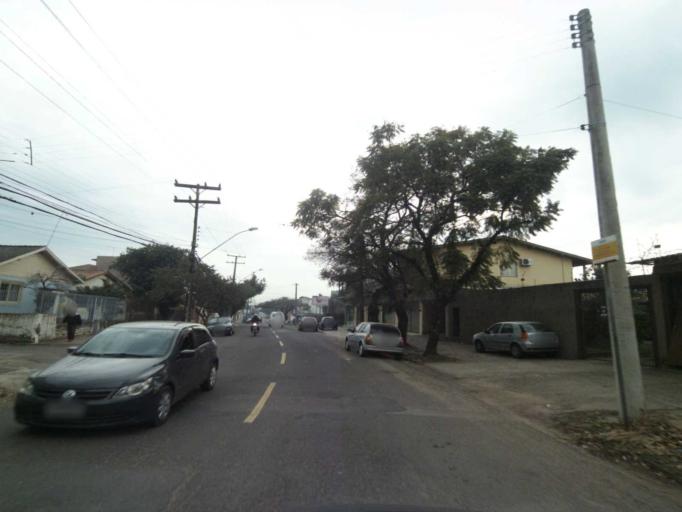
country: BR
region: Rio Grande do Sul
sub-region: Sao Leopoldo
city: Sao Leopoldo
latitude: -29.7771
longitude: -51.1564
